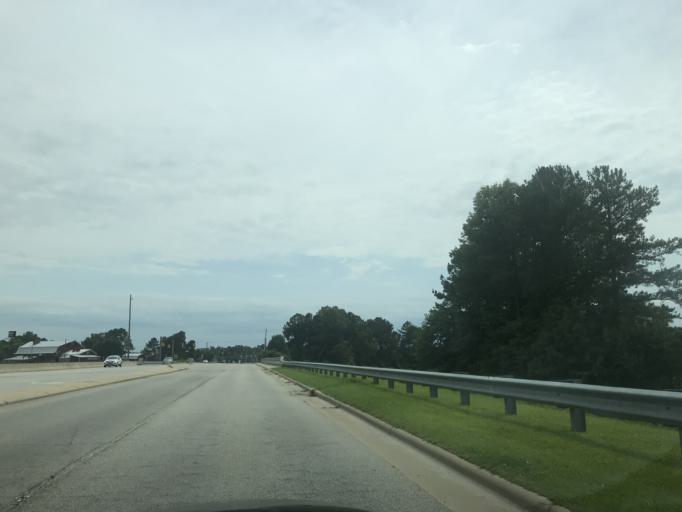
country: US
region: North Carolina
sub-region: Vance County
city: South Henderson
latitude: 36.3280
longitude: -78.4490
